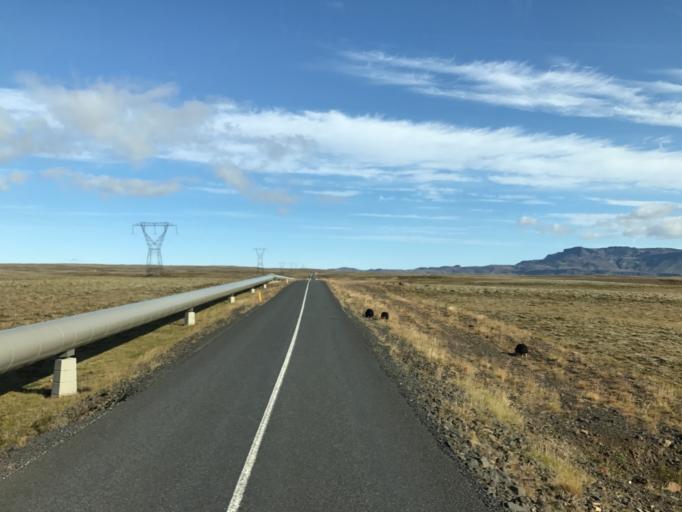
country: IS
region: Capital Region
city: Mosfellsbaer
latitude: 64.1132
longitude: -21.5225
